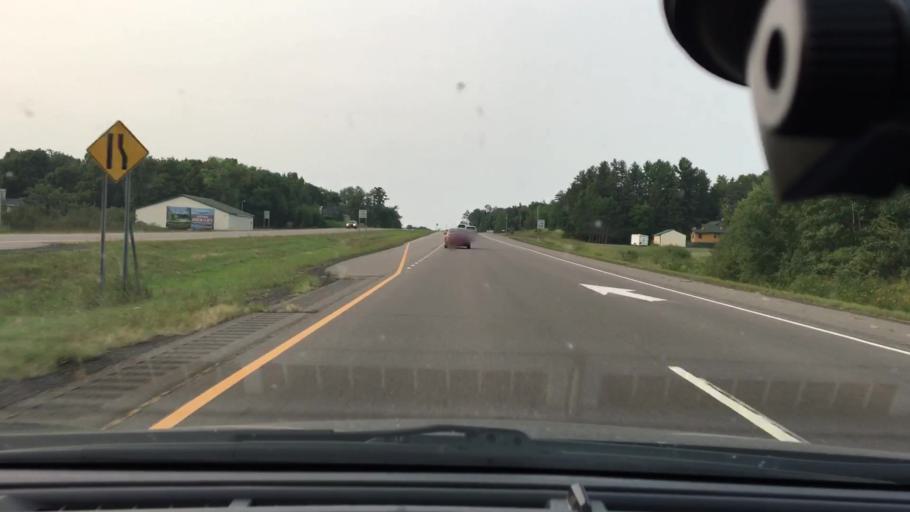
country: US
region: Minnesota
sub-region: Mille Lacs County
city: Vineland
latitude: 46.0998
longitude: -93.6445
